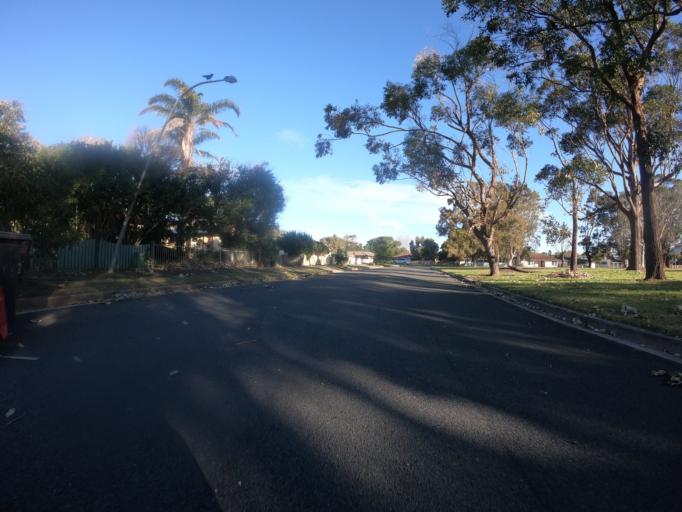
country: AU
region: New South Wales
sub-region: Wollongong
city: East Corrimal
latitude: -34.3679
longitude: 150.9216
